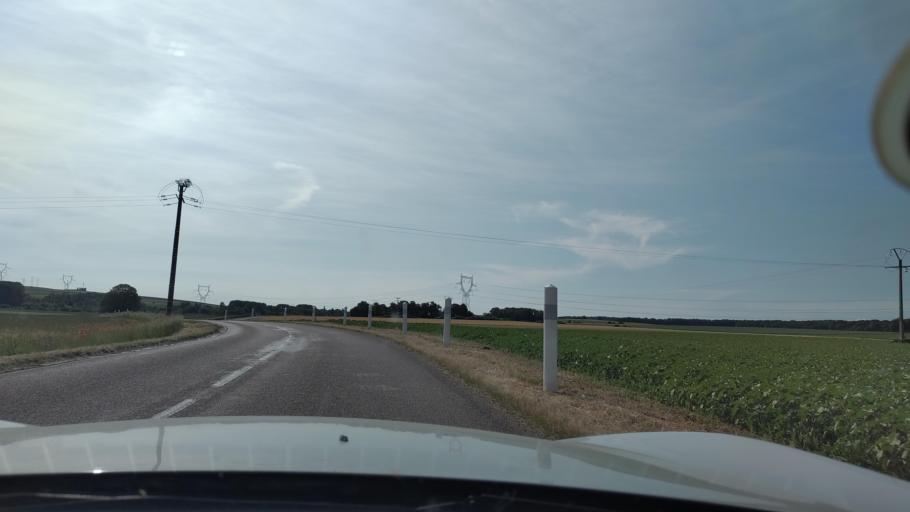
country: FR
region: Champagne-Ardenne
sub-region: Departement de l'Aube
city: Nogent-sur-Seine
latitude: 48.4618
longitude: 3.5882
